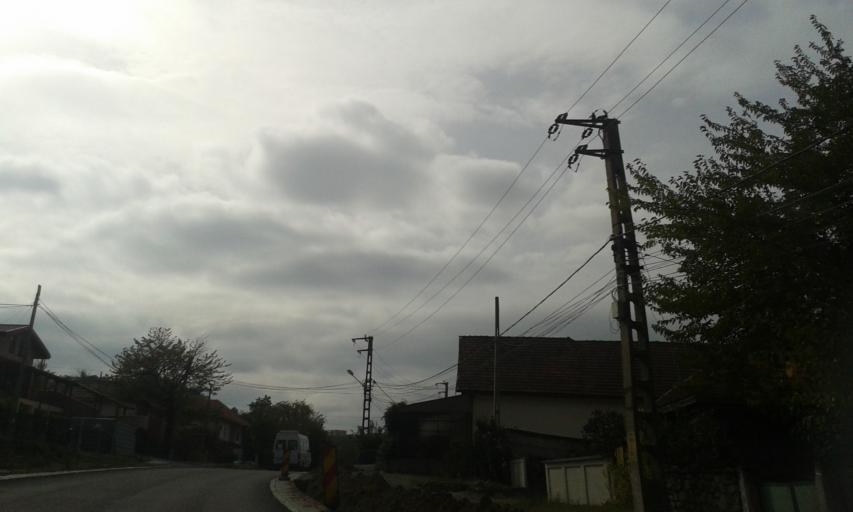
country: RO
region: Gorj
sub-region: Comuna Bumbesti-Jiu
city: Bumbesti-Jiu
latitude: 45.1867
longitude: 23.3871
